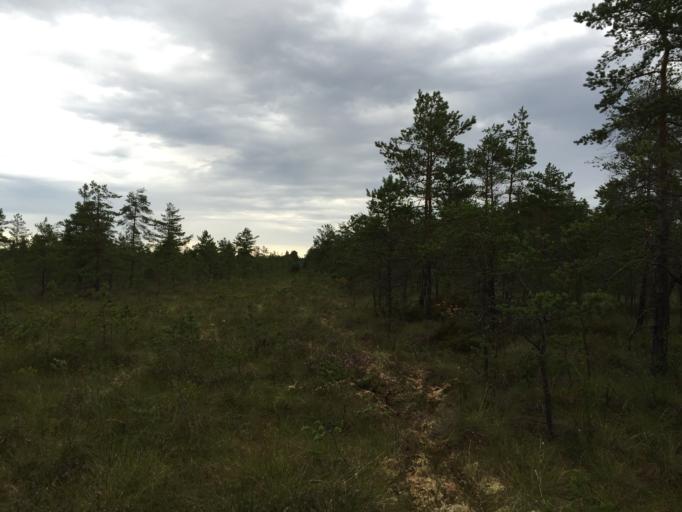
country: LV
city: Tireli
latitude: 56.8541
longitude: 23.6648
